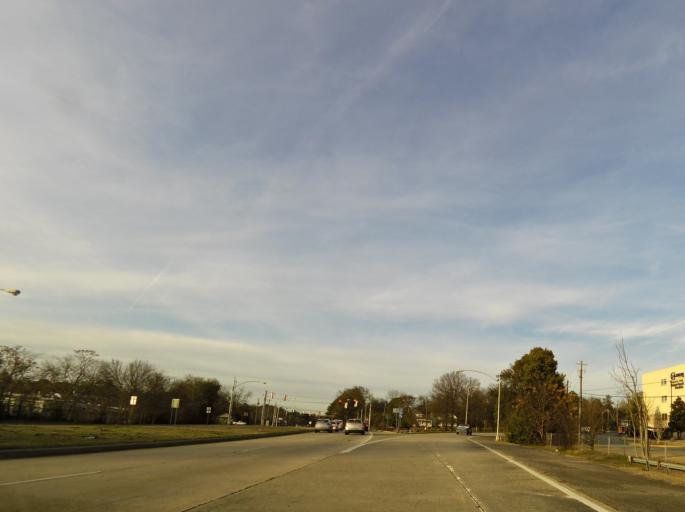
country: US
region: Georgia
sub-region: Bibb County
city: Macon
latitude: 32.8464
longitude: -83.6211
